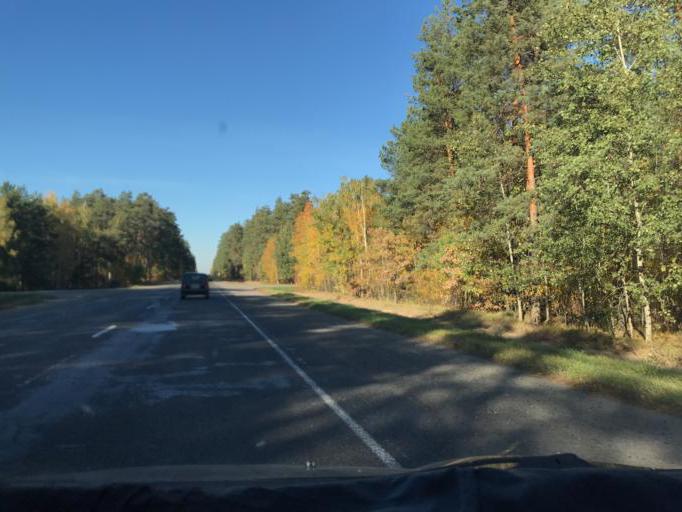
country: BY
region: Gomel
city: Kalinkavichy
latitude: 52.0551
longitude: 29.3611
